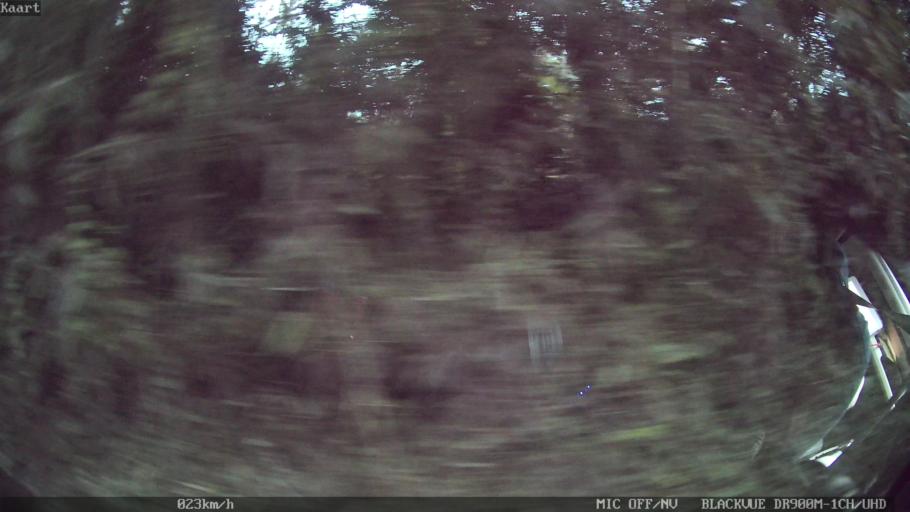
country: ID
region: Bali
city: Banjar Wangsian
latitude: -8.4534
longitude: 115.4189
